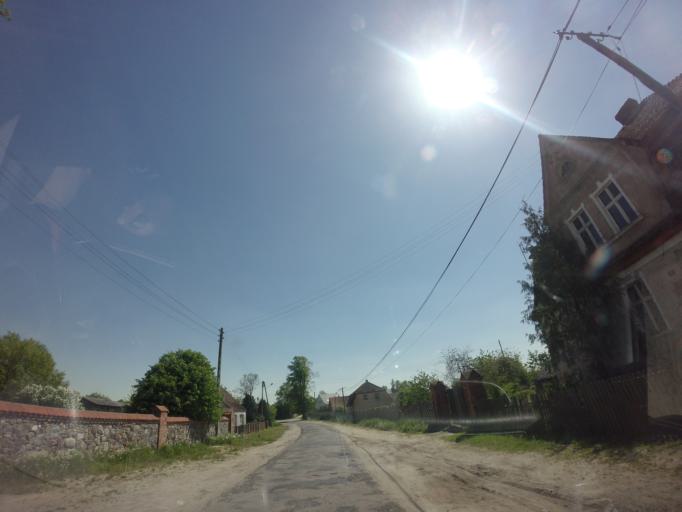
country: PL
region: West Pomeranian Voivodeship
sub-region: Powiat mysliborski
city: Nowogrodek Pomorski
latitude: 52.9100
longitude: 15.0310
